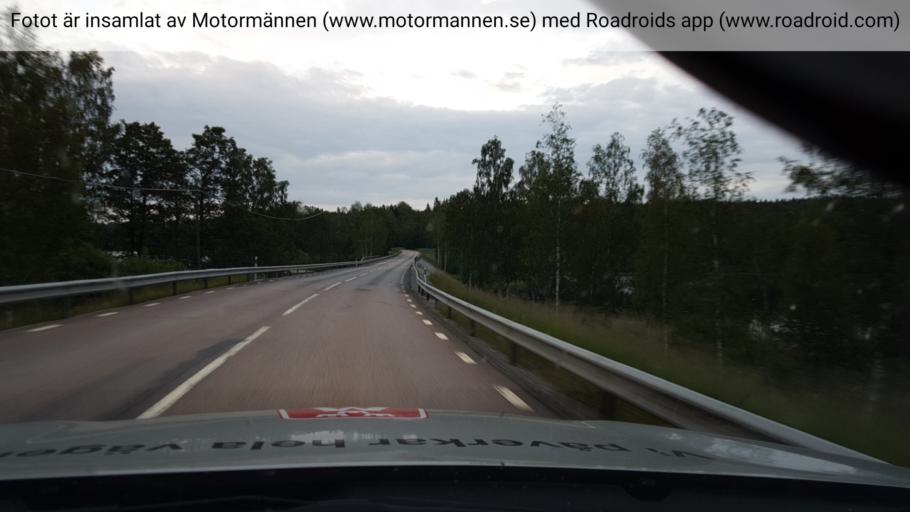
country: SE
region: Vaestmanland
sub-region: Skinnskattebergs Kommun
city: Skinnskatteberg
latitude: 59.8796
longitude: 15.6620
